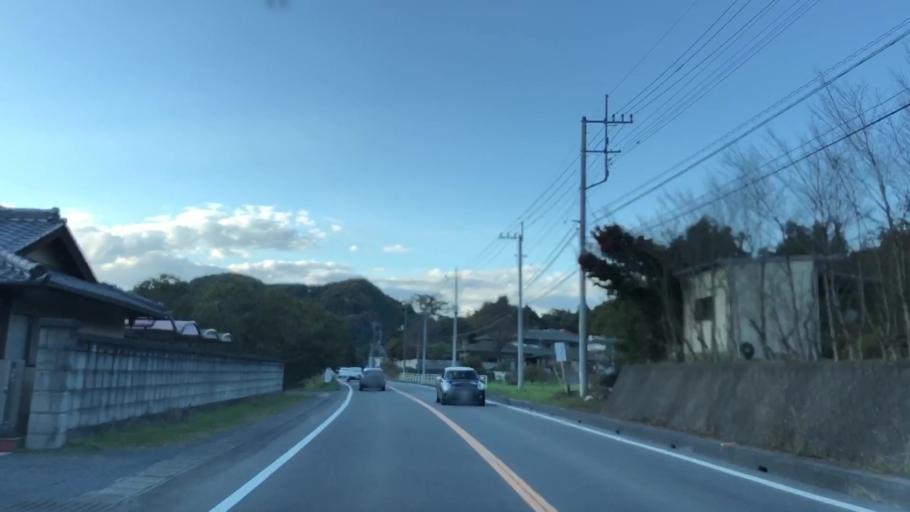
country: JP
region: Ibaraki
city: Kasama
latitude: 36.4813
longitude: 140.2938
